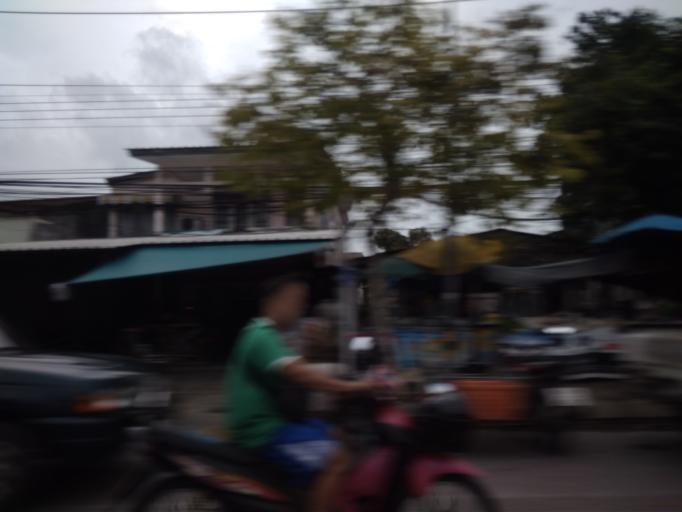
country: TH
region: Phuket
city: Mueang Phuket
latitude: 7.8615
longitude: 98.3805
